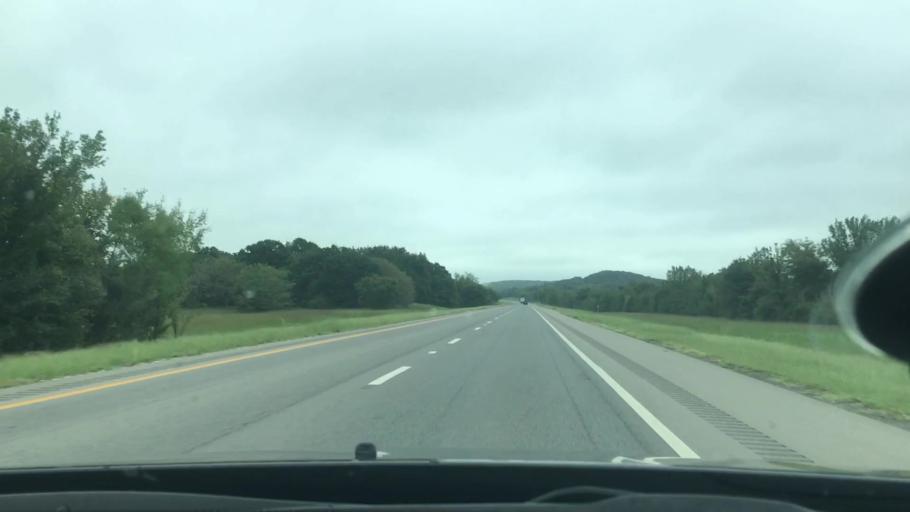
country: US
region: Oklahoma
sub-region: McIntosh County
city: Checotah
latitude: 35.4565
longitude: -95.4127
